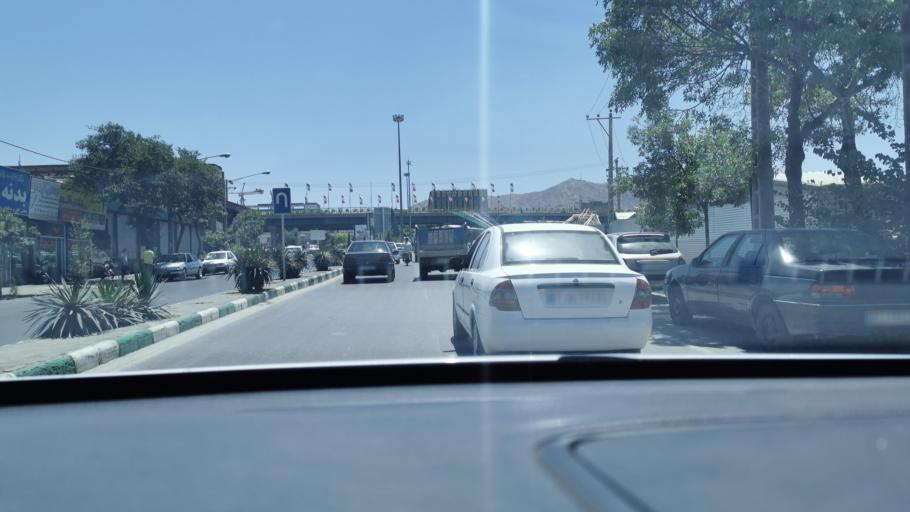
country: IR
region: Razavi Khorasan
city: Mashhad
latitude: 36.2575
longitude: 59.6002
